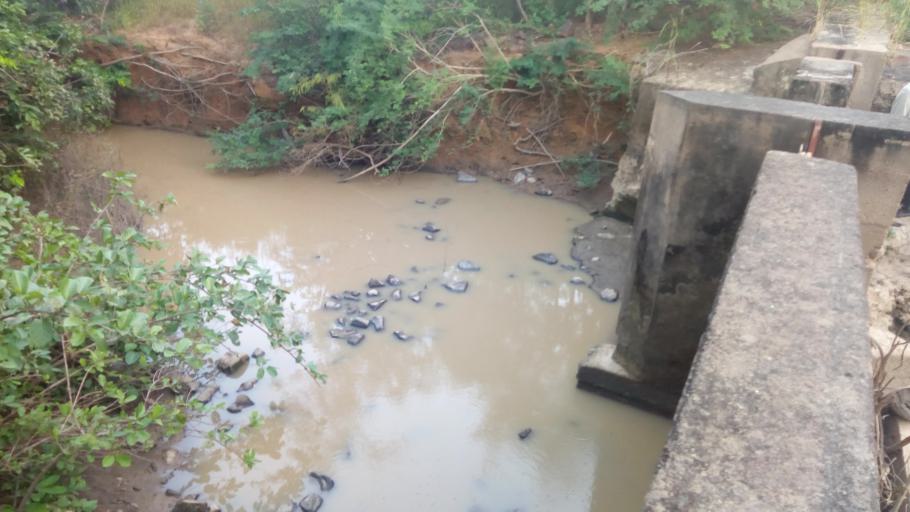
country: ML
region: Kayes
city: Kita
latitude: 13.1390
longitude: -8.8454
